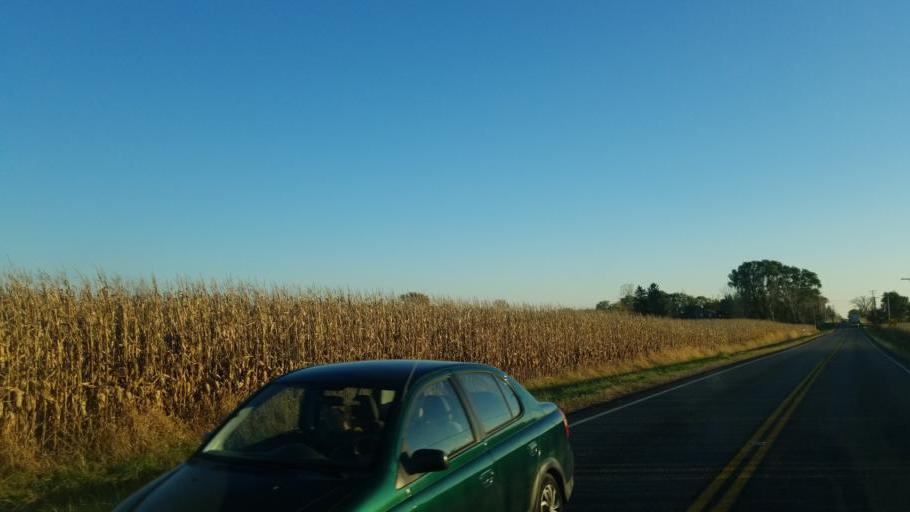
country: US
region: Ohio
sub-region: Sandusky County
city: Clyde
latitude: 41.2661
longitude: -82.9752
